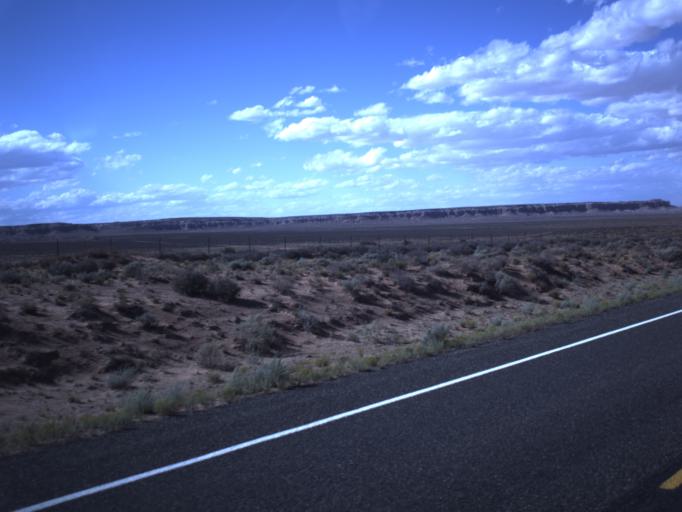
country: US
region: Utah
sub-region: Wayne County
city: Loa
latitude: 38.1642
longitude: -110.6227
